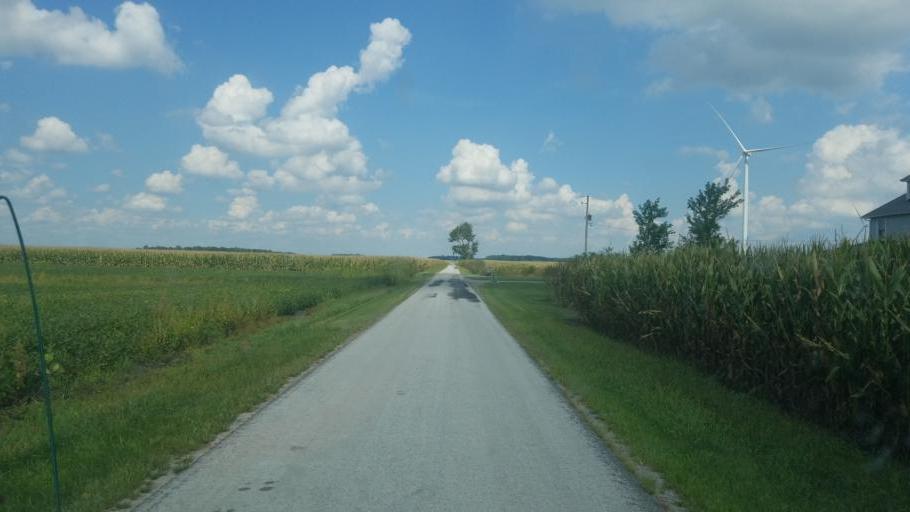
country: US
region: Ohio
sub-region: Hardin County
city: Ada
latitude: 40.7827
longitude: -83.7479
